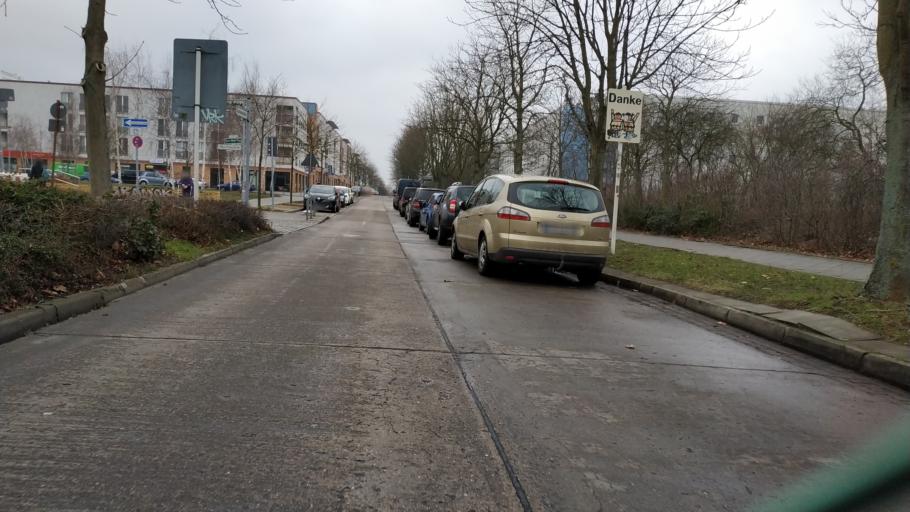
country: DE
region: Berlin
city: Hellersdorf
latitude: 52.5391
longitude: 13.6006
